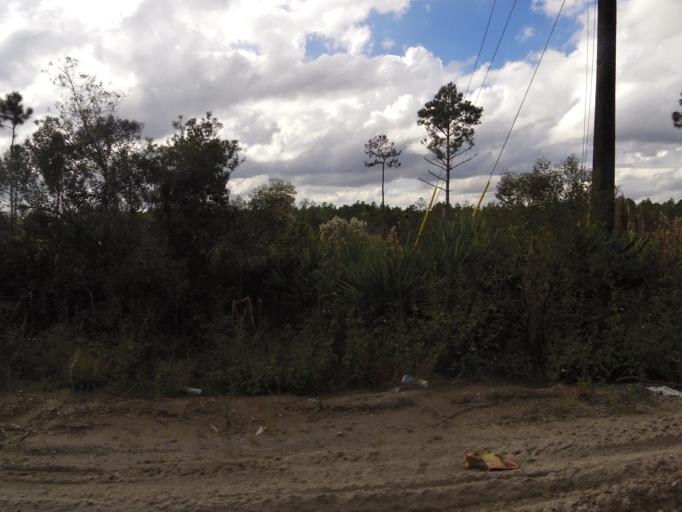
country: US
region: Florida
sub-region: Saint Johns County
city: Villano Beach
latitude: 29.9855
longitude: -81.3876
